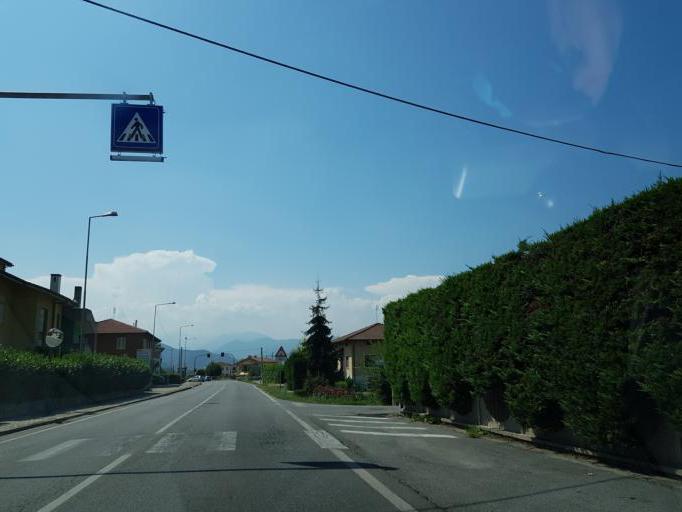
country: IT
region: Piedmont
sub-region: Provincia di Cuneo
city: San Rocco
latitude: 44.3977
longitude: 7.4766
